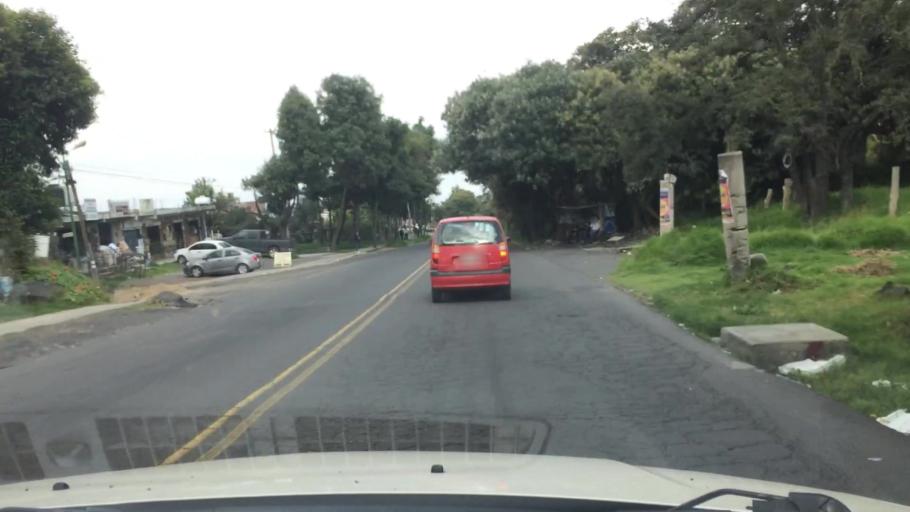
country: MX
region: Mexico City
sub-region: Tlalpan
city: Lomas de Tepemecatl
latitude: 19.2686
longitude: -99.2177
